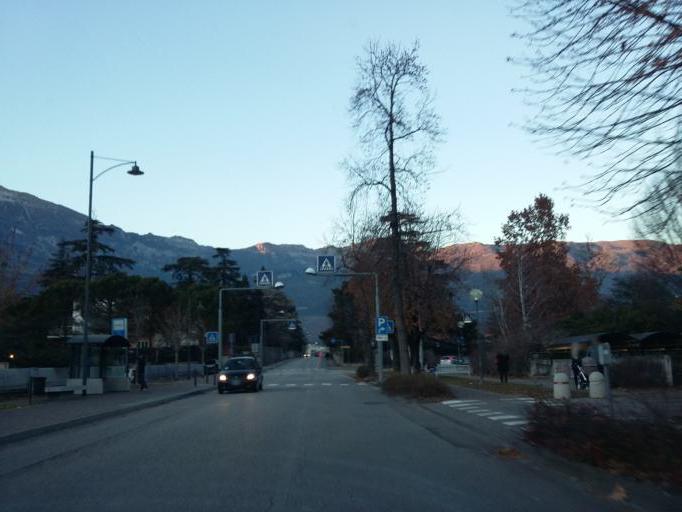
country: IT
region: Trentino-Alto Adige
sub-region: Provincia di Trento
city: Villa Lagarina
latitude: 45.9014
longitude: 11.0416
